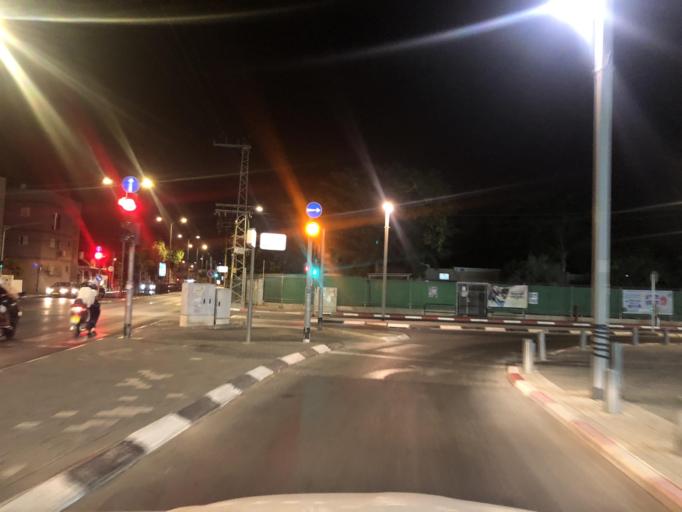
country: IL
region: Tel Aviv
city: Azor
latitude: 32.0473
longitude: 34.7916
